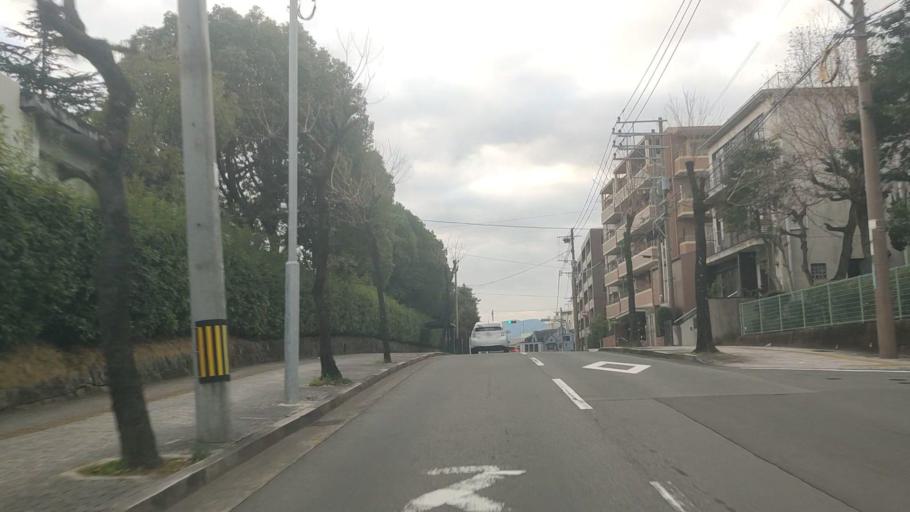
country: JP
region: Nagasaki
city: Nagasaki-shi
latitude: 32.7733
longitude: 129.8673
